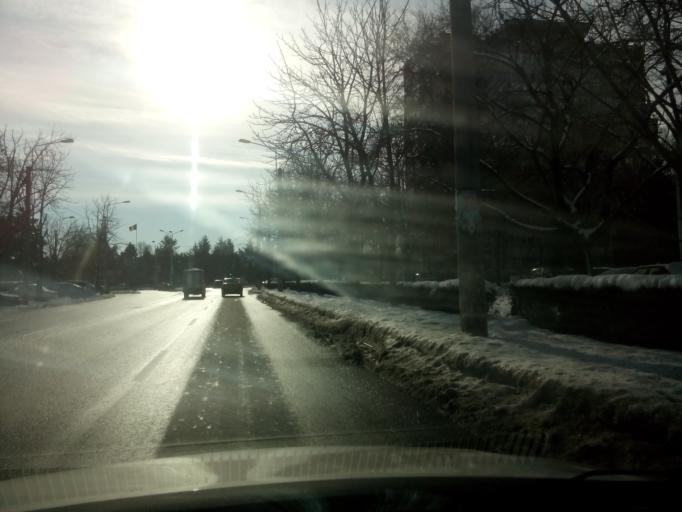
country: RO
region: Ilfov
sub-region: Comuna Fundeni-Dobroesti
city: Fundeni
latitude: 44.4244
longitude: 26.1503
